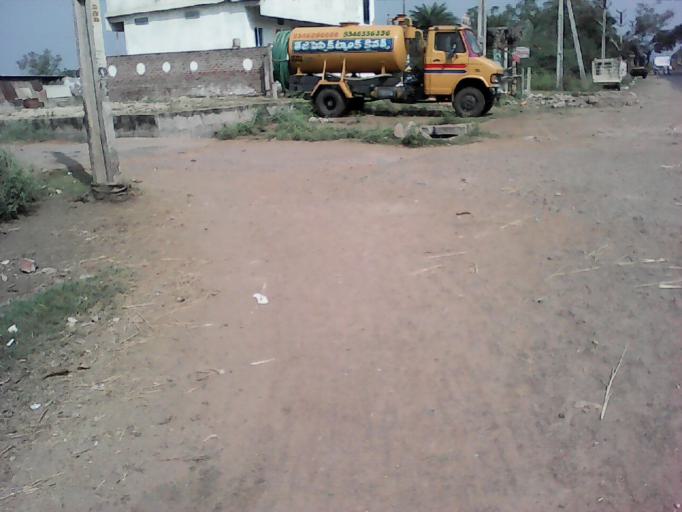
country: IN
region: Andhra Pradesh
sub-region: Guntur
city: Bhattiprolu
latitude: 16.2376
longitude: 80.6610
